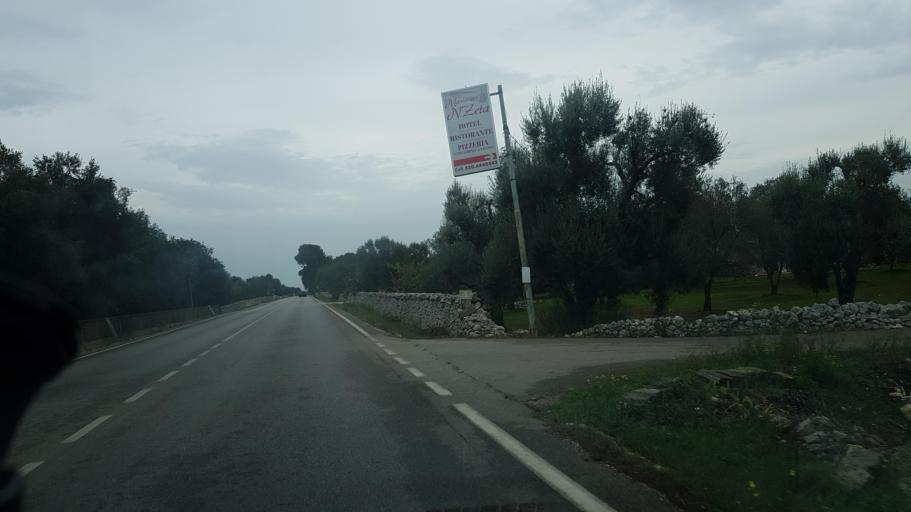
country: IT
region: Apulia
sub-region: Provincia di Brindisi
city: Carovigno
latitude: 40.7124
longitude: 17.6309
